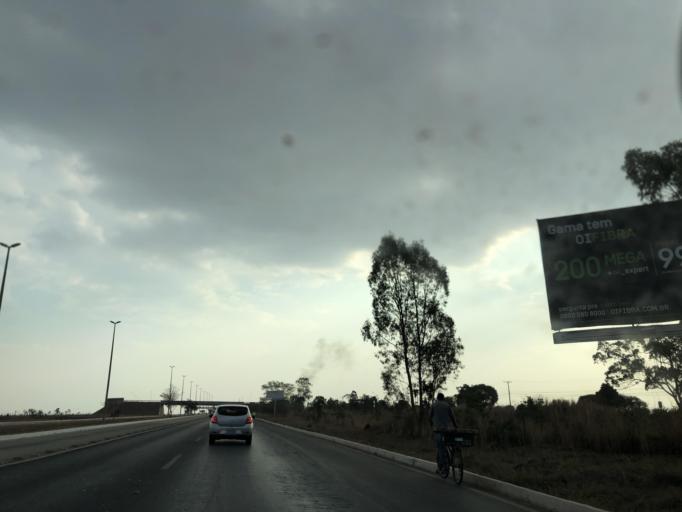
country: BR
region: Federal District
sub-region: Brasilia
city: Brasilia
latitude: -15.9506
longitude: -48.0037
